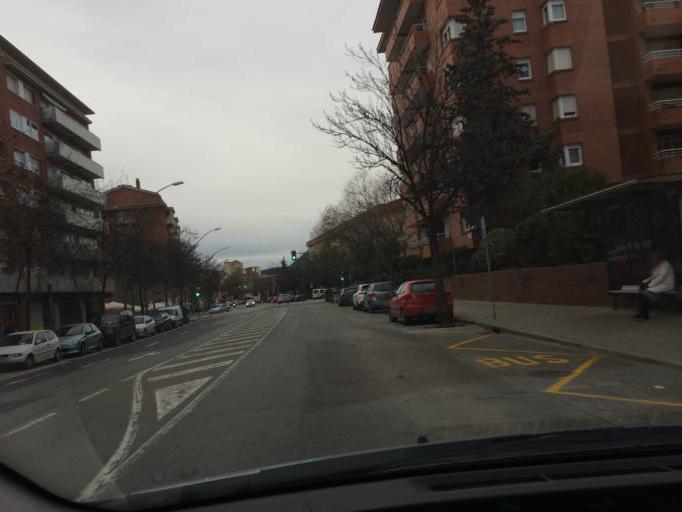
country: ES
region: Catalonia
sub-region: Provincia de Barcelona
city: Manresa
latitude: 41.7367
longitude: 1.8310
